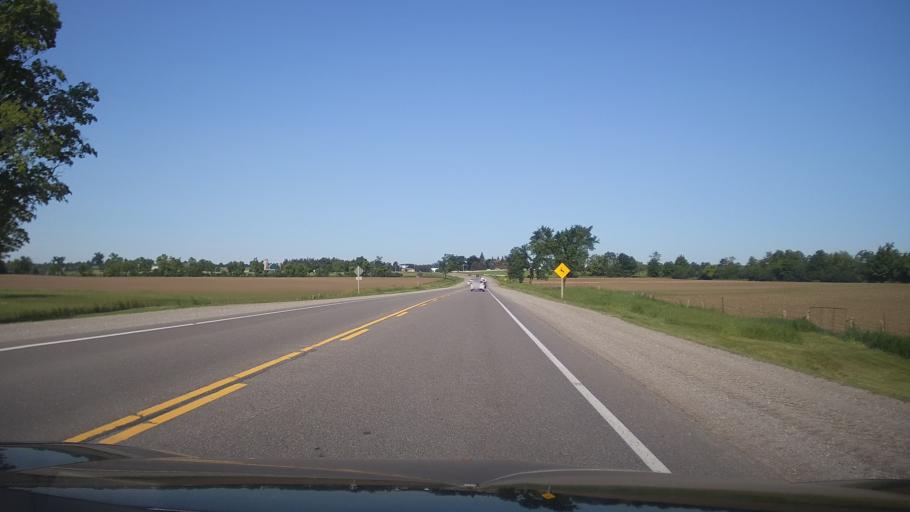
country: CA
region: Ontario
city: Omemee
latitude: 44.3466
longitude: -78.8140
